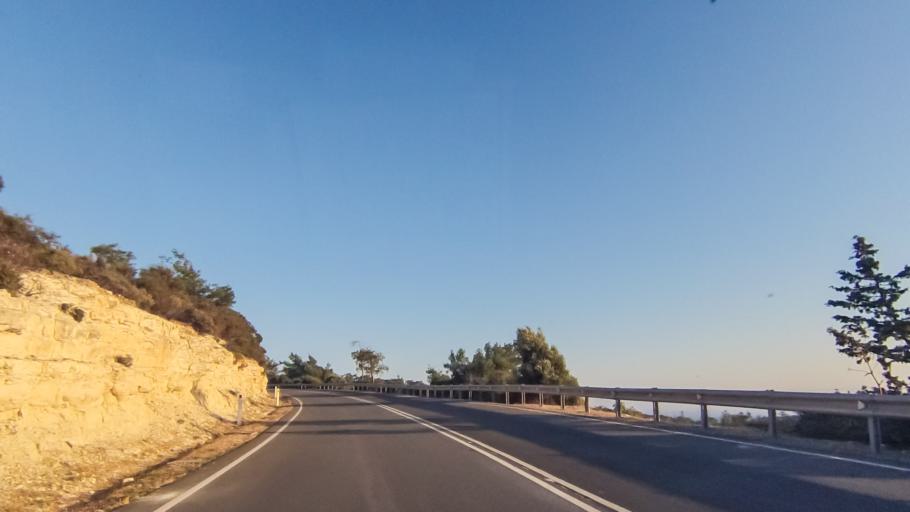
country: CY
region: Limassol
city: Sotira
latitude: 34.6756
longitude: 32.8517
